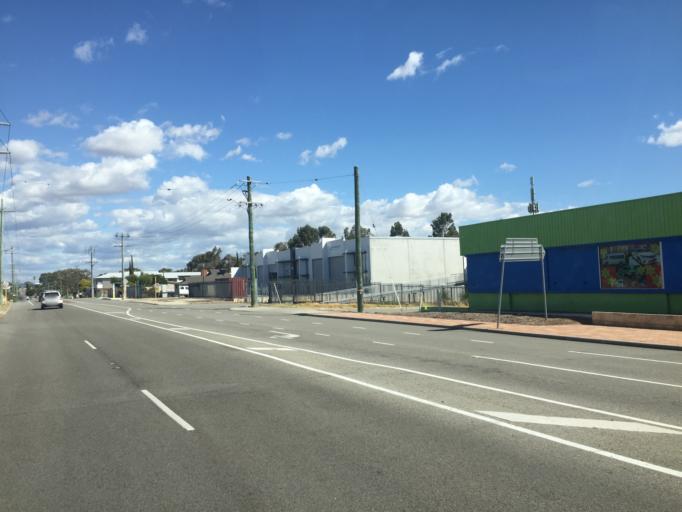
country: AU
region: Western Australia
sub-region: Belmont
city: Belmont
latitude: -31.9410
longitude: 115.9275
